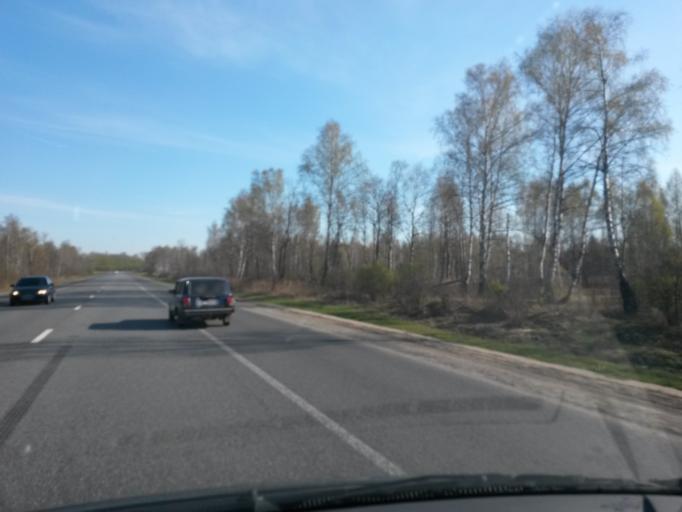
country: RU
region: Jaroslavl
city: Porech'ye-Rybnoye
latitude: 57.1168
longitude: 39.3196
